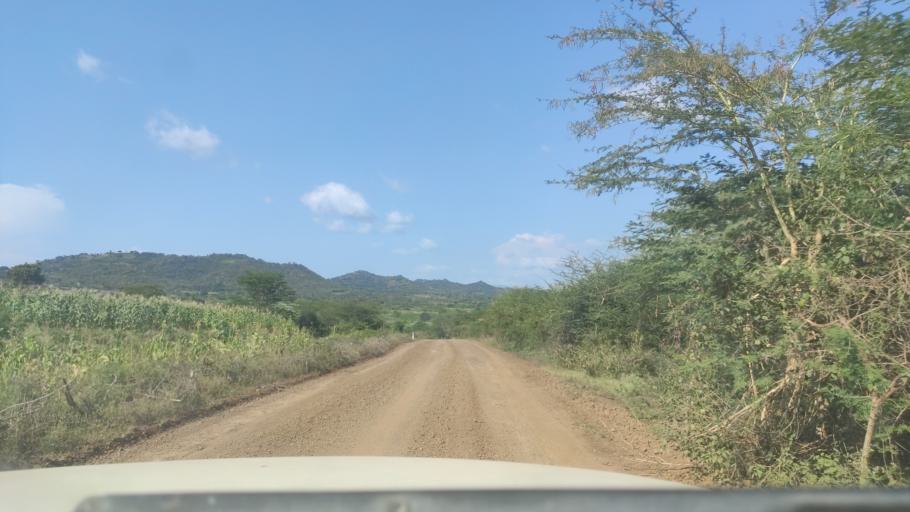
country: ET
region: Southern Nations, Nationalities, and People's Region
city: Felege Neway
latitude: 6.3855
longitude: 37.0955
